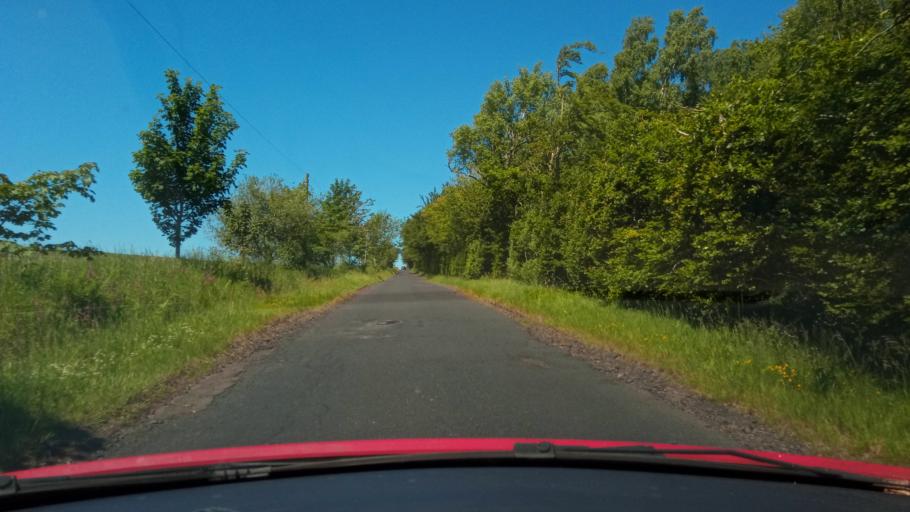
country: GB
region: Scotland
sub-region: The Scottish Borders
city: Duns
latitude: 55.8135
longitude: -2.4976
